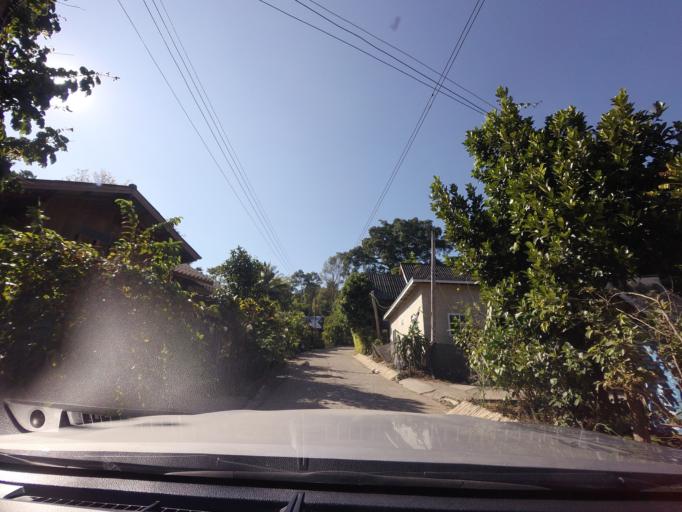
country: TH
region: Lampang
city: Mueang Pan
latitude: 18.8288
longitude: 99.3844
